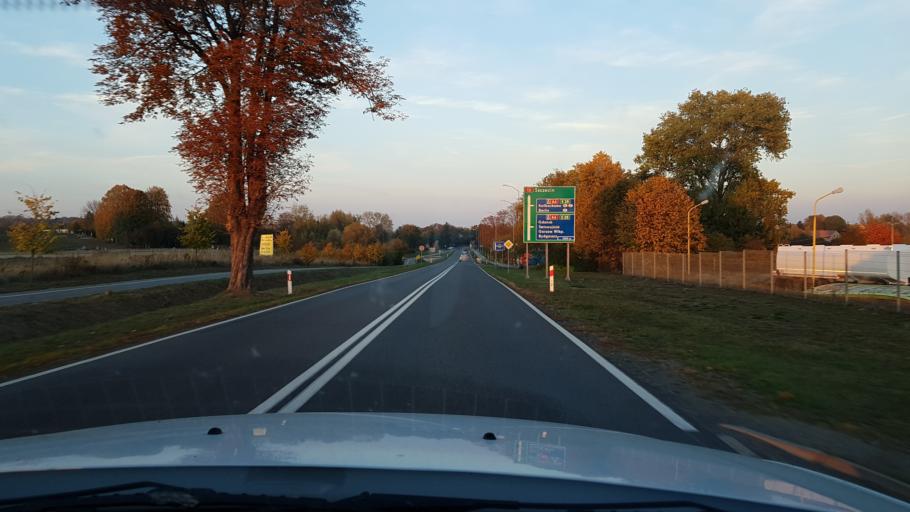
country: PL
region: West Pomeranian Voivodeship
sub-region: Powiat policki
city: Kolbaskowo
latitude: 53.3331
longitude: 14.4321
